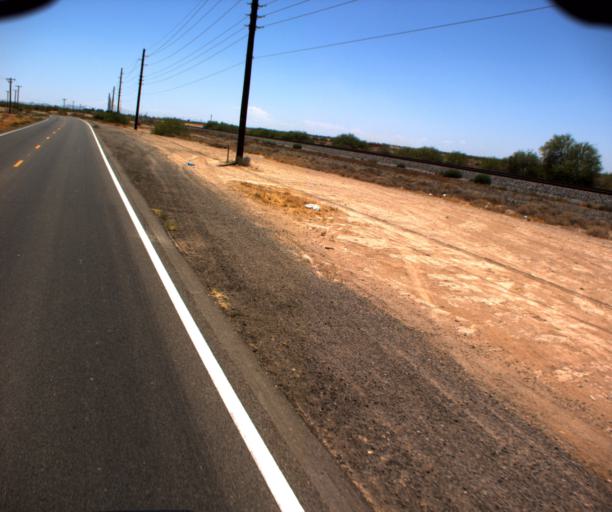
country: US
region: Arizona
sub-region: Pinal County
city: Maricopa
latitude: 33.0737
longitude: -112.0825
